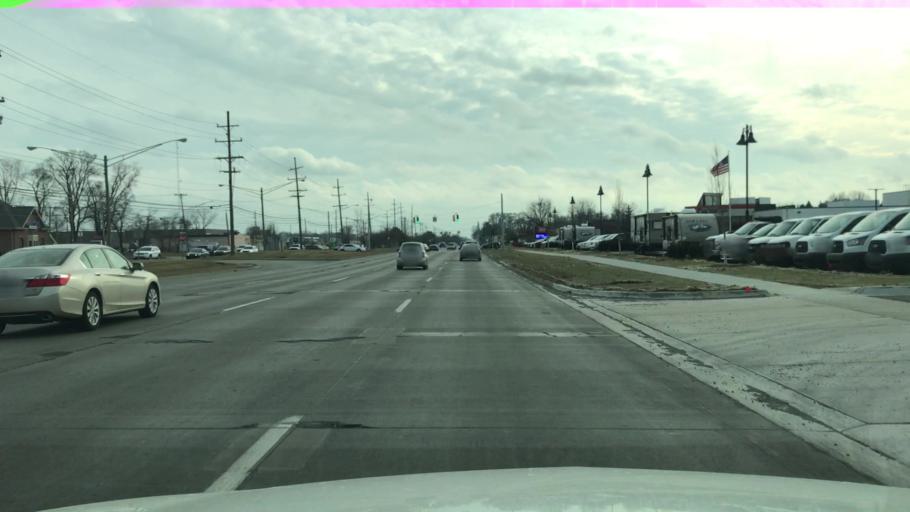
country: US
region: Michigan
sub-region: Macomb County
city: Sterling Heights
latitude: 42.5538
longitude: -83.0488
